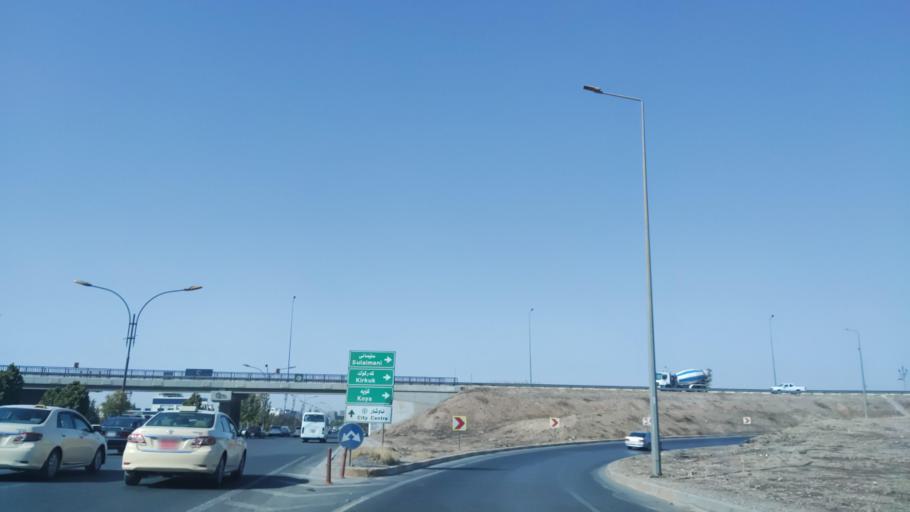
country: IQ
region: Arbil
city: Erbil
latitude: 36.2320
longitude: 44.0551
